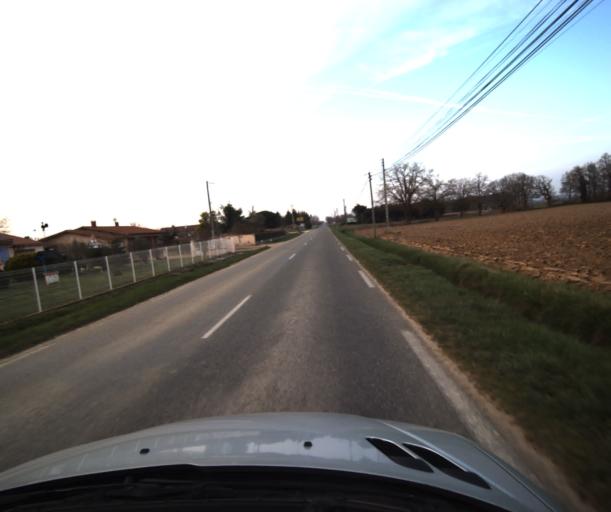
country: FR
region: Midi-Pyrenees
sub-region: Departement de la Haute-Garonne
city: Fronton
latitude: 43.8534
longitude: 1.3858
